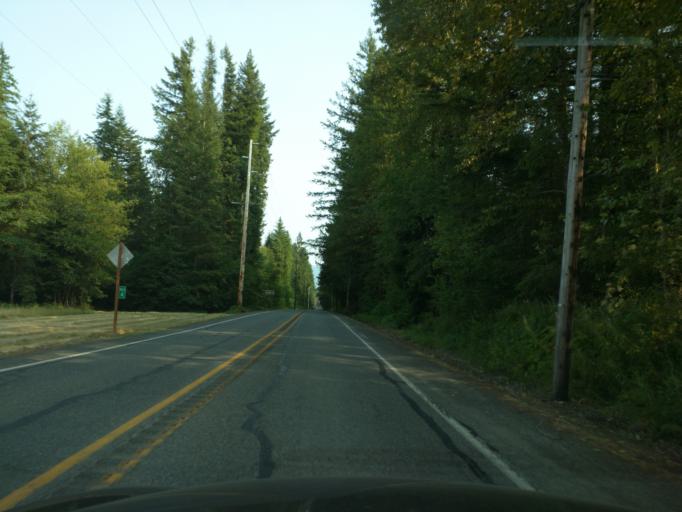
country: US
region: Washington
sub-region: Whatcom County
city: Peaceful Valley
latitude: 48.9670
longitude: -122.1628
